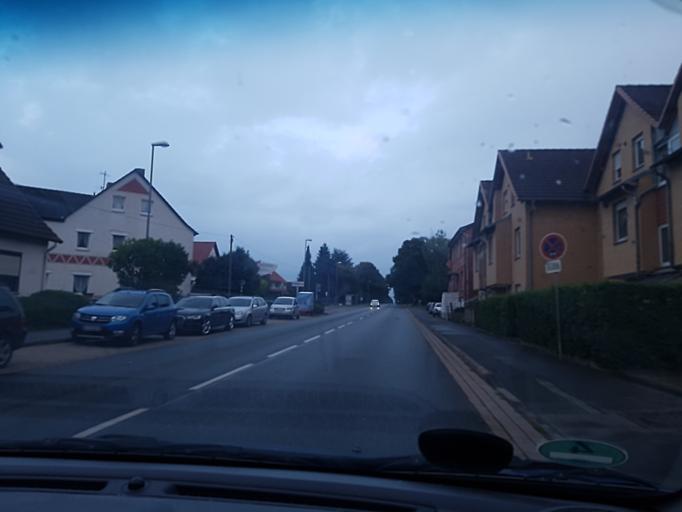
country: DE
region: Lower Saxony
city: Hemmingen
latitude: 52.2988
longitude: 9.7412
